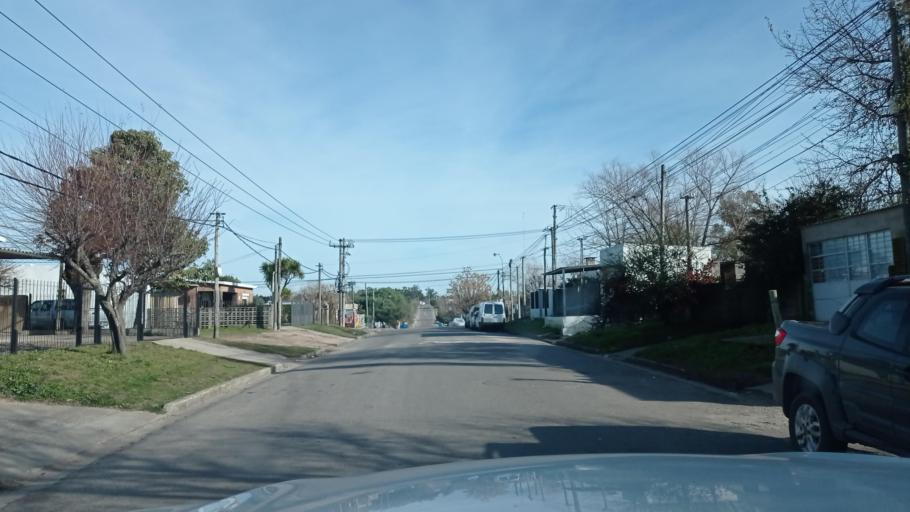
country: UY
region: Florida
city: Florida
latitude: -34.0896
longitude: -56.2327
